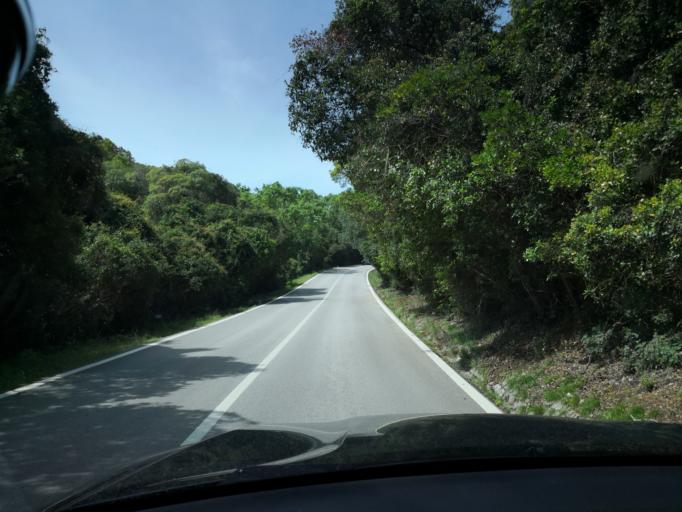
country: PT
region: Setubal
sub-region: Sesimbra
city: Sesimbra
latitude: 38.4619
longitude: -9.0030
